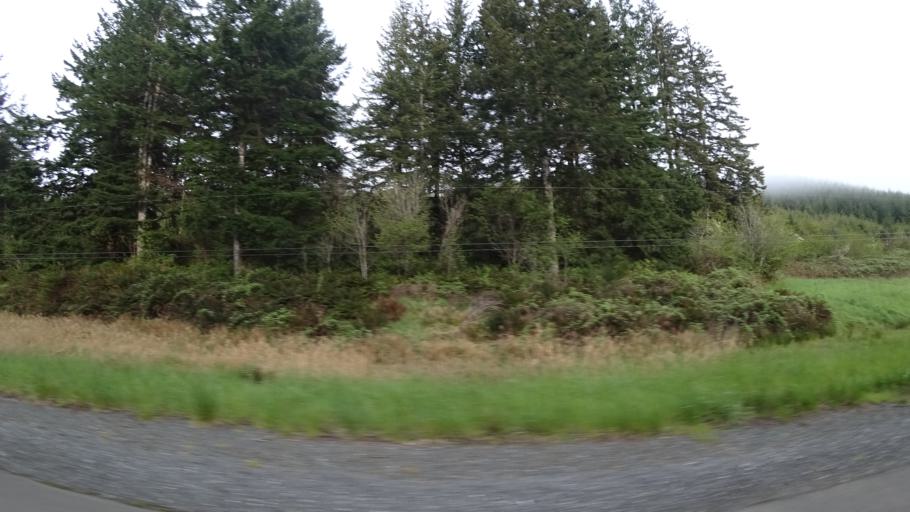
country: US
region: Oregon
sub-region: Coos County
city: Barview
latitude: 43.2765
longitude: -124.2599
